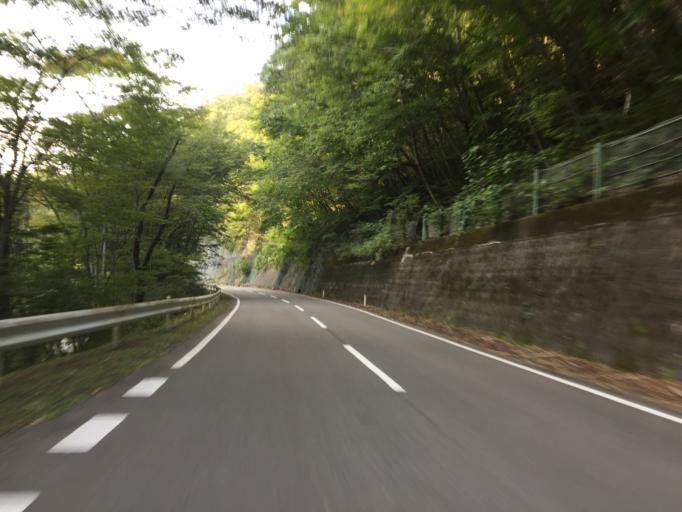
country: JP
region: Fukushima
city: Namie
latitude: 37.5565
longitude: 140.8327
